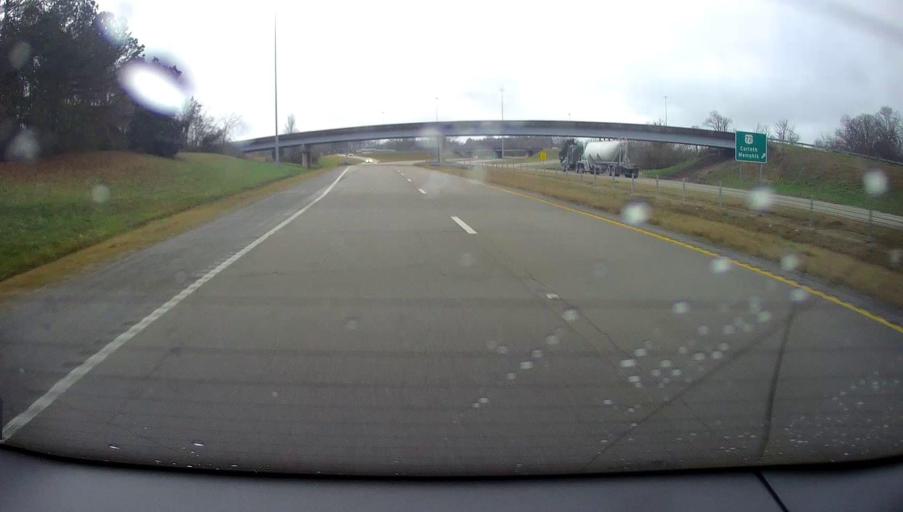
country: US
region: Mississippi
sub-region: Alcorn County
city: Corinth
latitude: 34.9271
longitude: -88.5460
